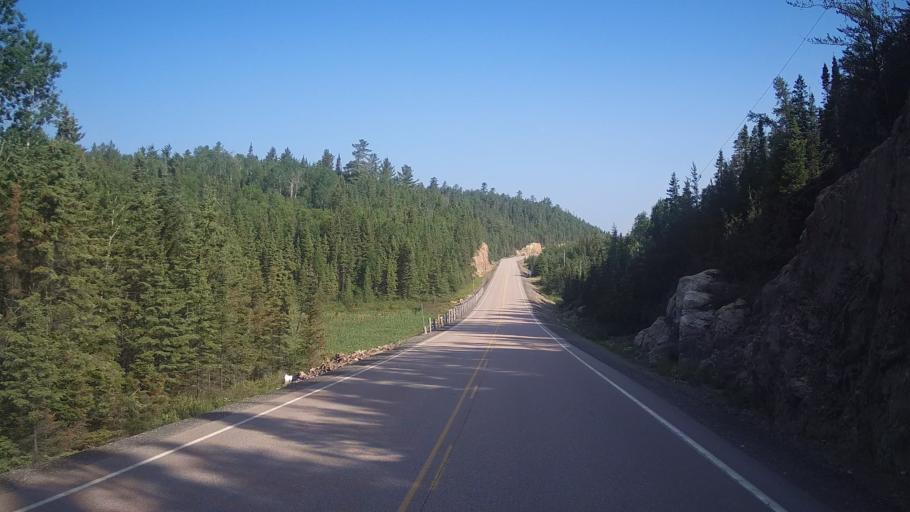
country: CA
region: Ontario
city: Rayside-Balfour
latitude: 47.0139
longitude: -81.6347
